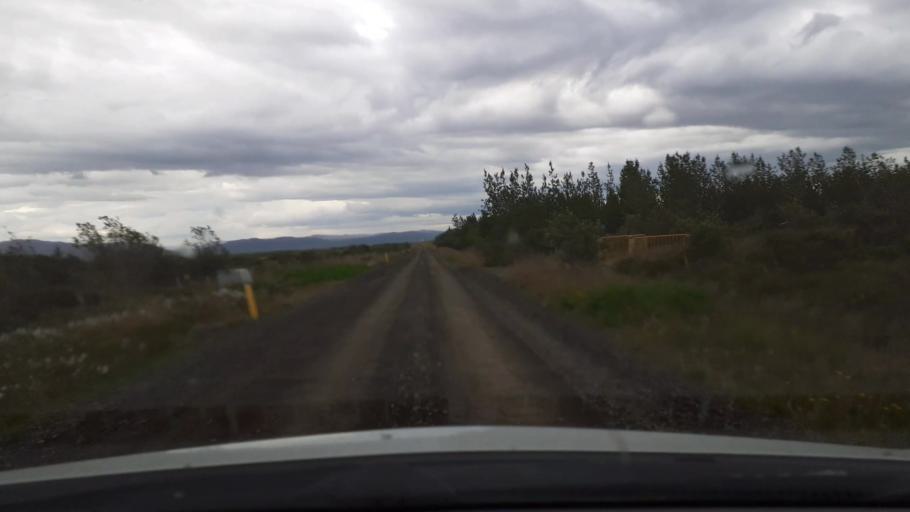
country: IS
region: West
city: Borgarnes
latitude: 64.6259
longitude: -21.9297
